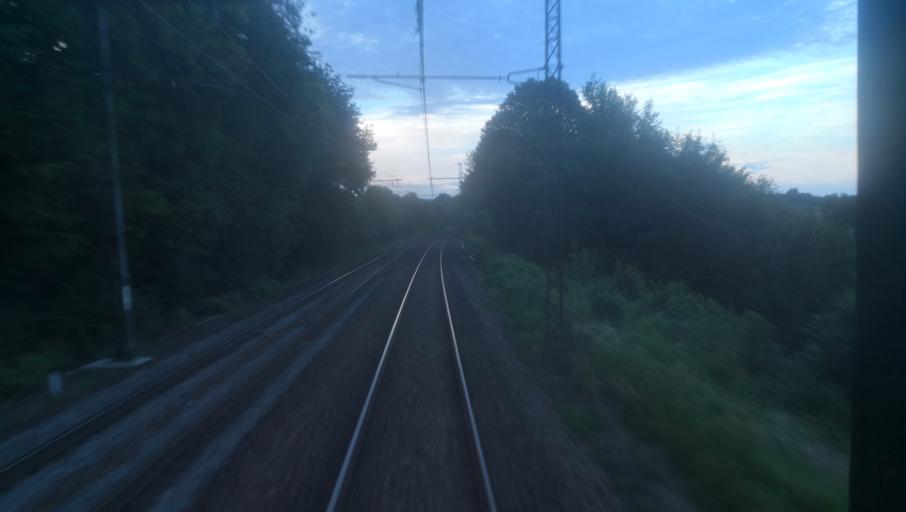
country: FR
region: Limousin
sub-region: Departement de la Haute-Vienne
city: Ambazac
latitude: 45.9897
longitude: 1.4732
